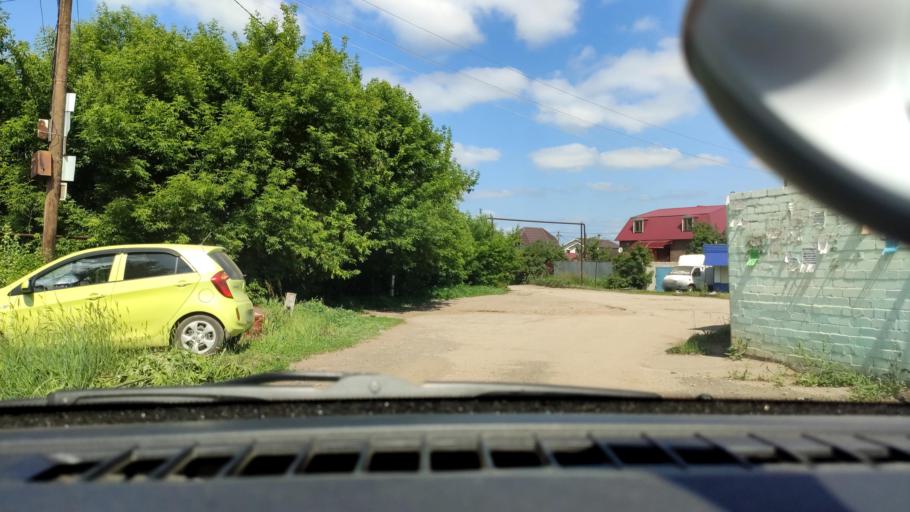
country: RU
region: Samara
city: Samara
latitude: 53.1296
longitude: 50.1781
